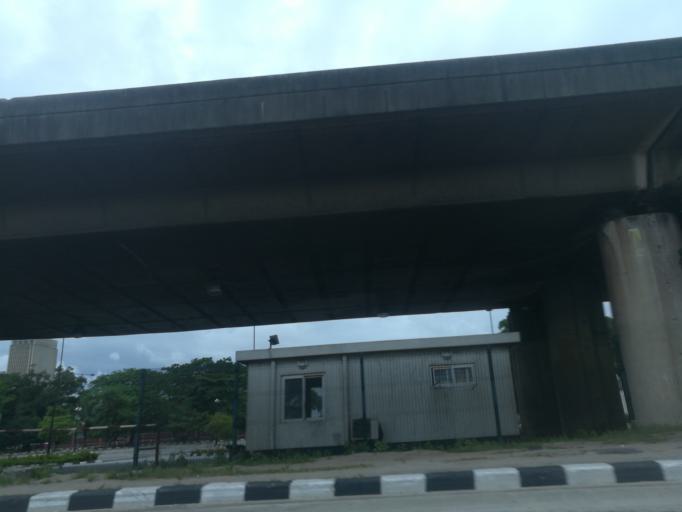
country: NG
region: Lagos
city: Lagos
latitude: 6.4441
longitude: 3.3983
